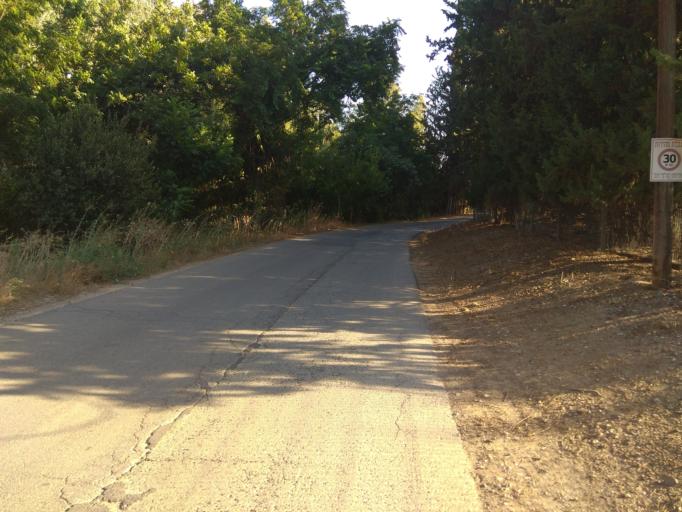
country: IL
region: Northern District
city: Qiryat Shemona
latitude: 33.2220
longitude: 35.6191
